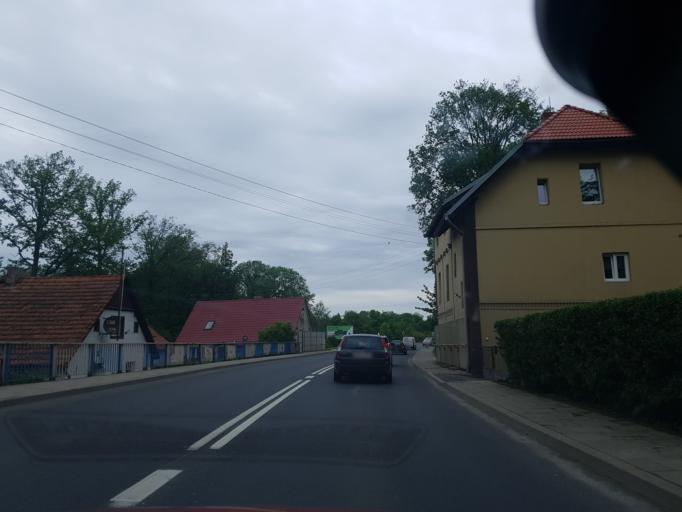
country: PL
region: Lower Silesian Voivodeship
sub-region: Powiat wroclawski
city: Gniechowice
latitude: 50.9863
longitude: 16.8272
